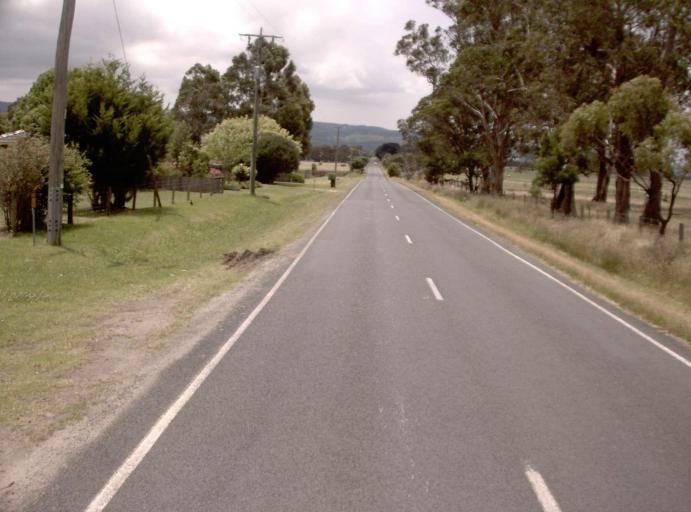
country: AU
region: Victoria
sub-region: Latrobe
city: Traralgon
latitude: -38.5290
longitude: 146.6591
